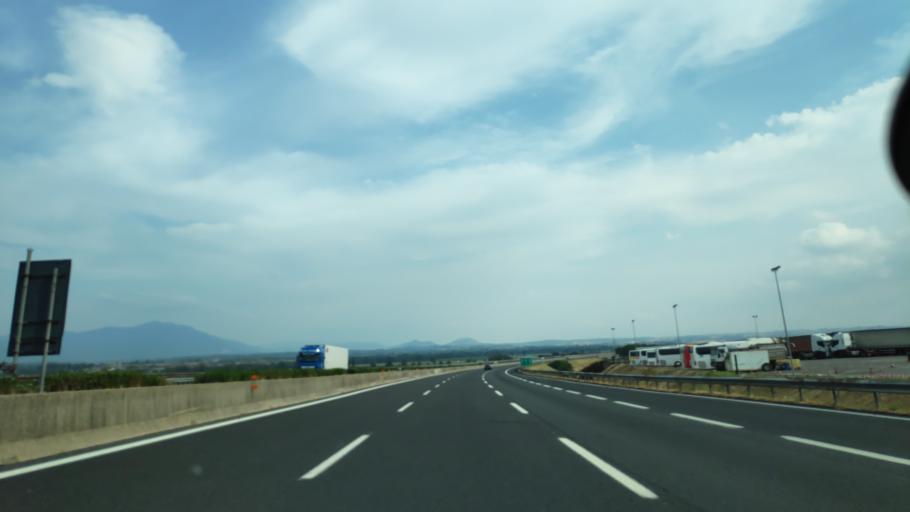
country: IT
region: Latium
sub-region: Citta metropolitana di Roma Capitale
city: Fiano Romano
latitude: 42.1589
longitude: 12.6221
